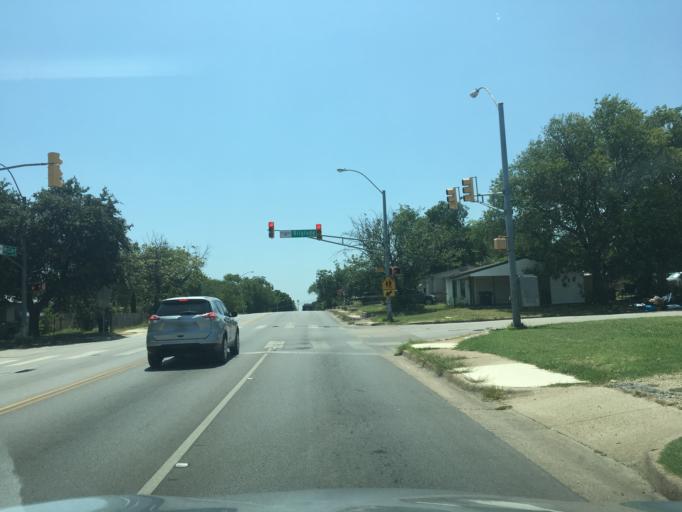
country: US
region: Texas
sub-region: Tarrant County
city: Edgecliff Village
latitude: 32.6775
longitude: -97.3531
